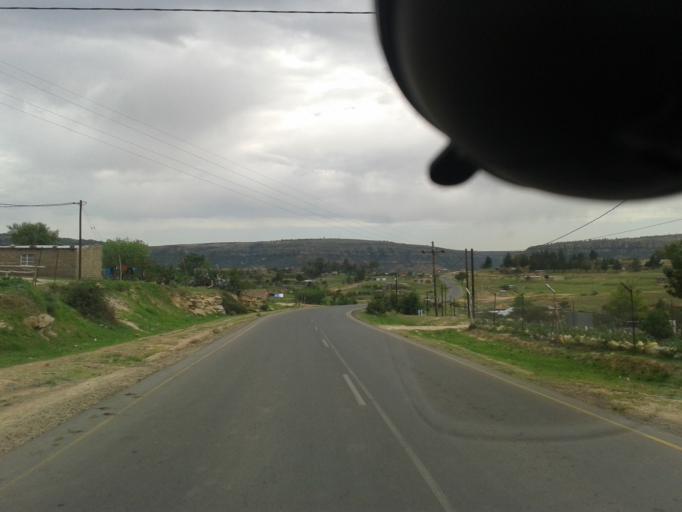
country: LS
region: Maseru
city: Maseru
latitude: -29.3580
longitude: 27.6520
